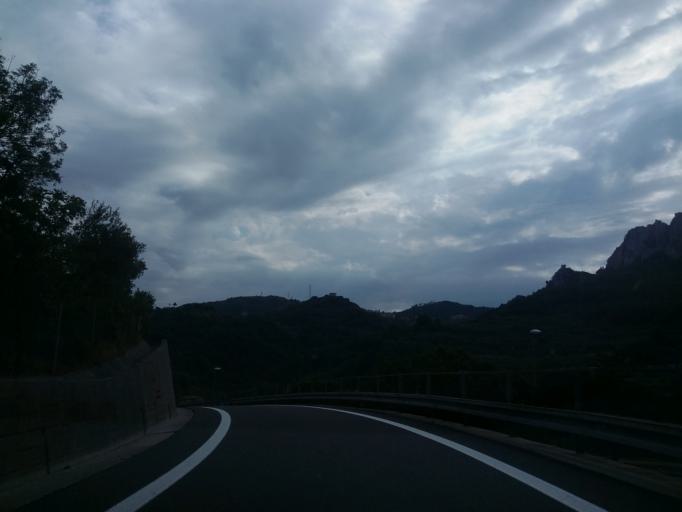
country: IT
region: Liguria
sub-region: Provincia di Savona
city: Feglino
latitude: 44.2137
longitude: 8.3214
